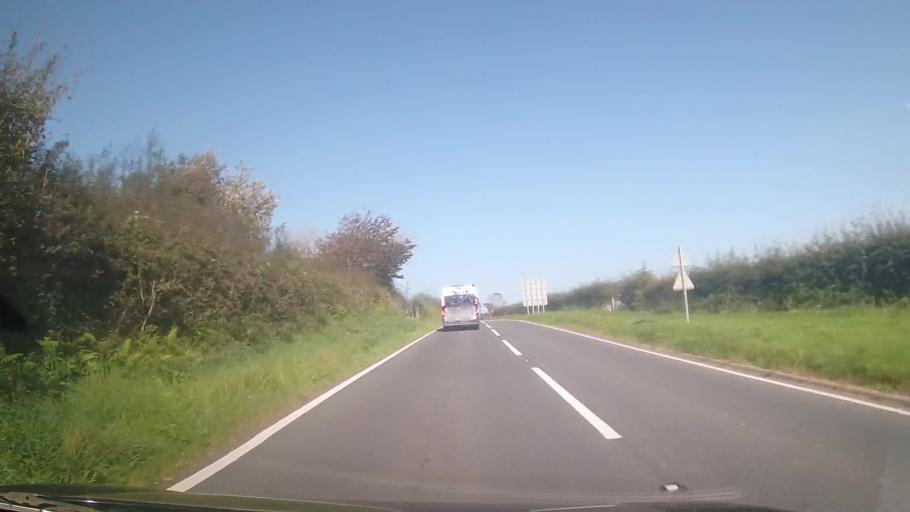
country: GB
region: Wales
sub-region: County of Ceredigion
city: Cardigan
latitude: 52.0551
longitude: -4.6899
